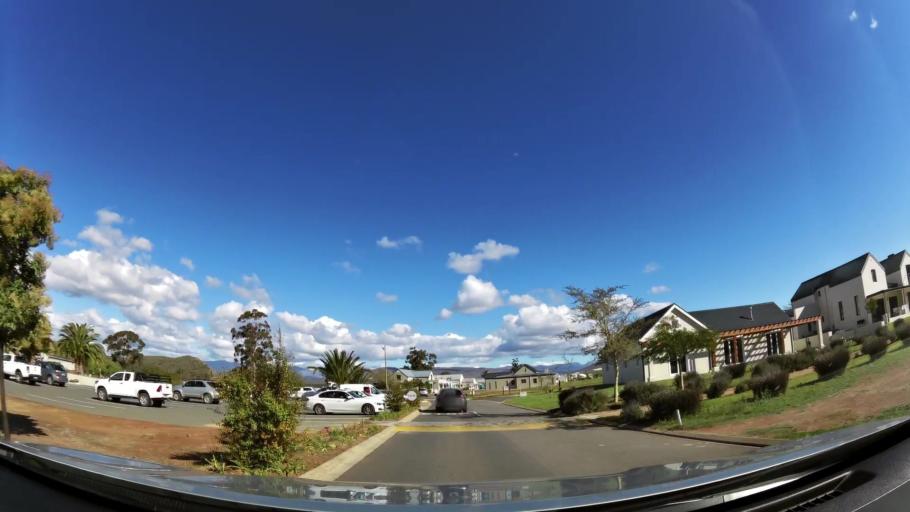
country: ZA
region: Western Cape
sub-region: Cape Winelands District Municipality
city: Ashton
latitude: -33.8100
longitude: 19.8511
